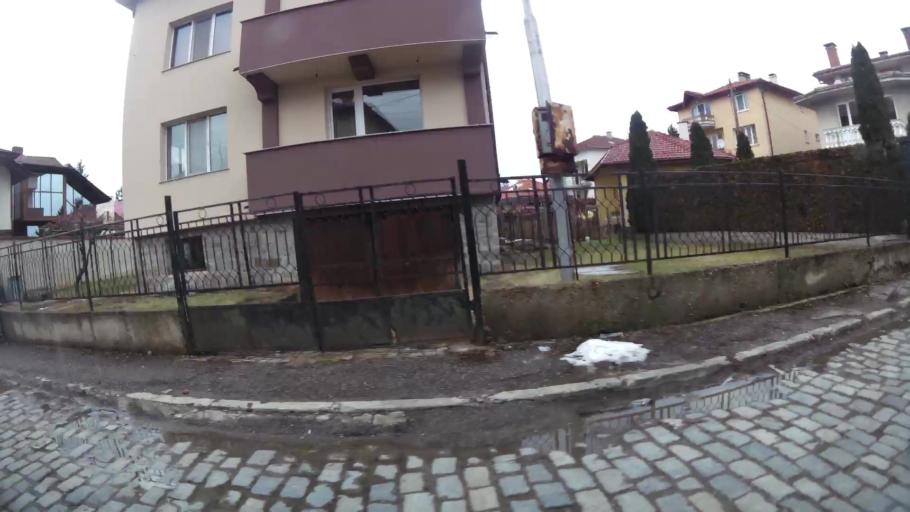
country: BG
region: Sofiya
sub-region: Obshtina Bozhurishte
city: Bozhurishte
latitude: 42.7434
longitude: 23.2662
